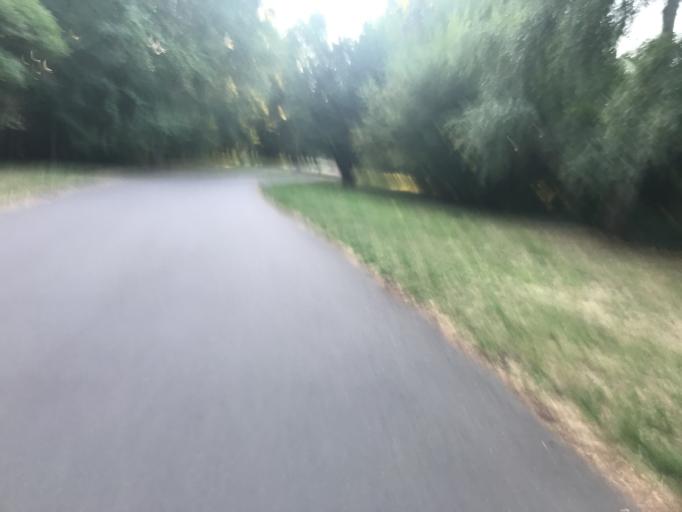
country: DE
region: Berlin
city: Plaenterwald
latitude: 52.4709
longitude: 13.4730
